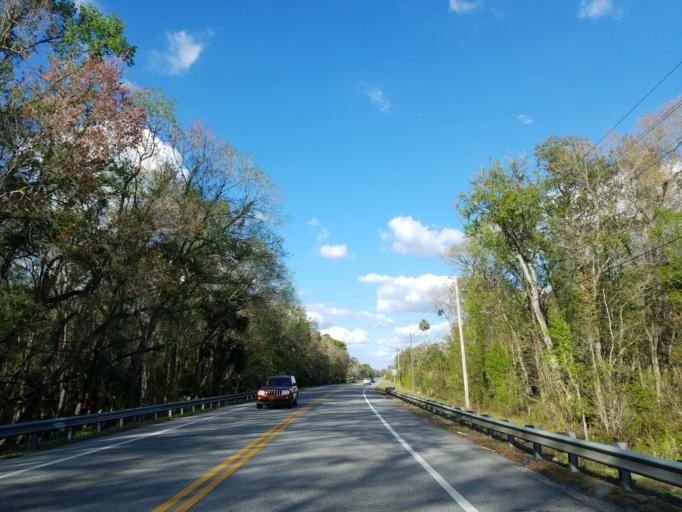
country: US
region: Florida
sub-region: Pasco County
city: Land O' Lakes
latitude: 28.2140
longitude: -82.3908
